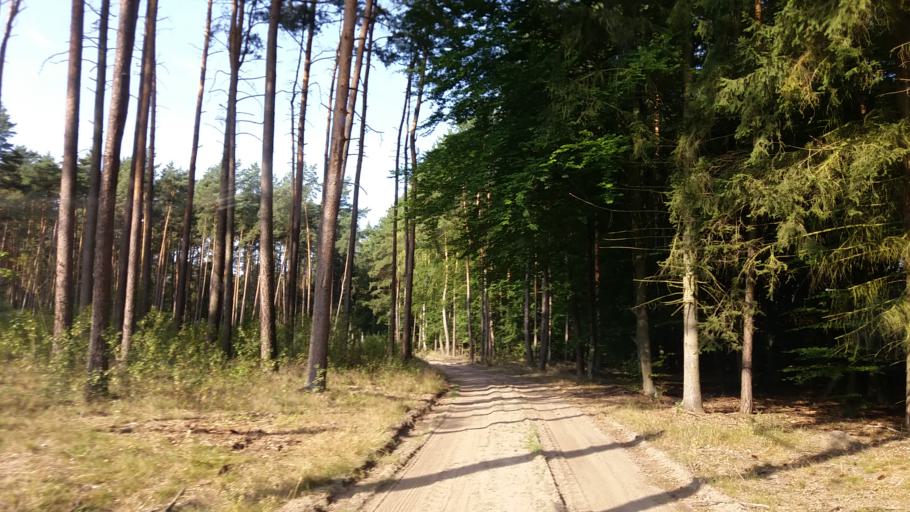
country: PL
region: West Pomeranian Voivodeship
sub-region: Powiat choszczenski
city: Choszczno
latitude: 53.2433
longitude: 15.4061
